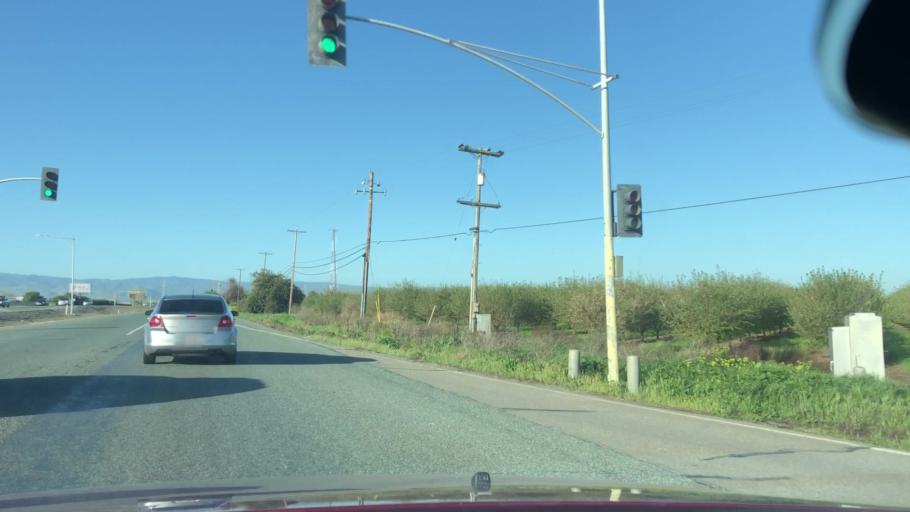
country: US
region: California
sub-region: San Joaquin County
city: Tracy
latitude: 37.7459
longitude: -121.3619
